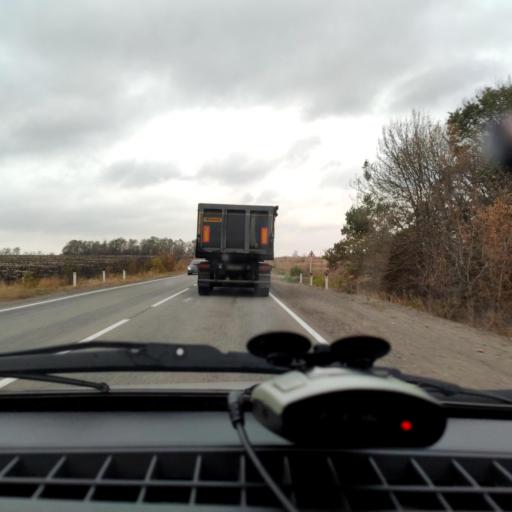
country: RU
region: Voronezj
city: Shilovo
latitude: 51.4562
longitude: 38.9735
